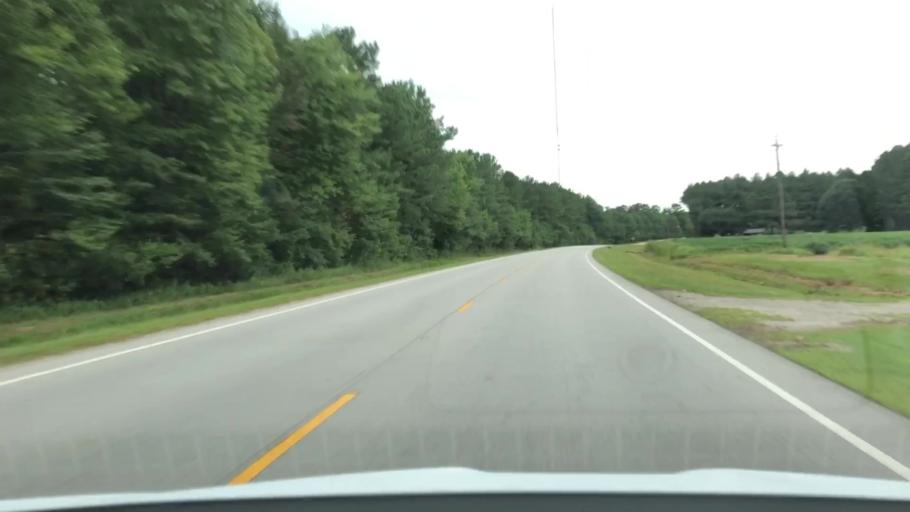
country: US
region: North Carolina
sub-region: Jones County
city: Trenton
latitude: 35.0373
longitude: -77.3447
